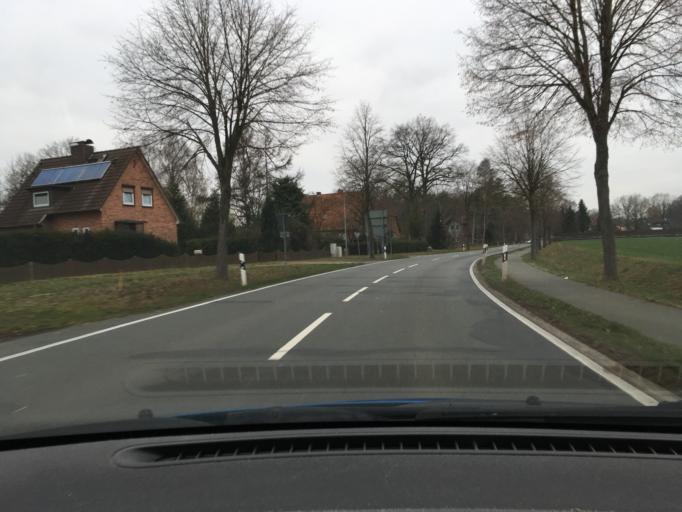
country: DE
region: Lower Saxony
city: Soltau
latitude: 52.9693
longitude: 9.8512
